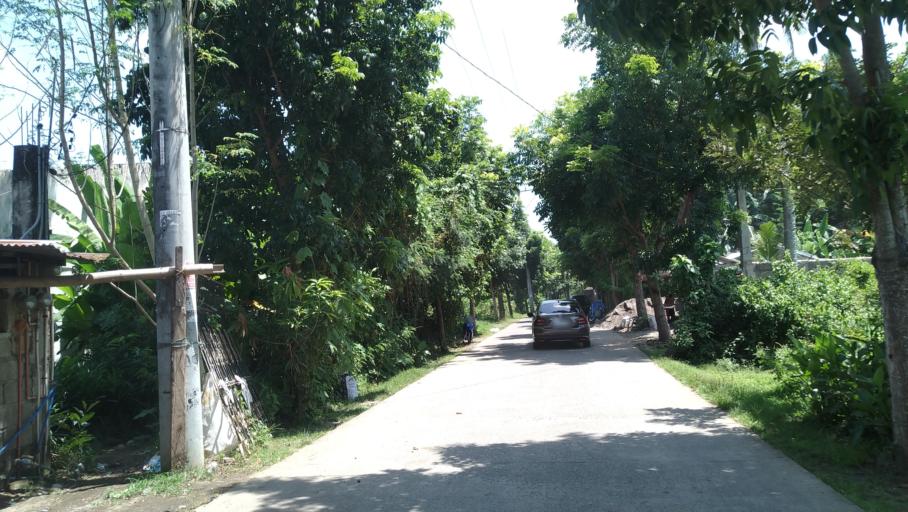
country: PH
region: Calabarzon
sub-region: Province of Laguna
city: Cabanbanan
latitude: 14.2494
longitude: 121.4162
